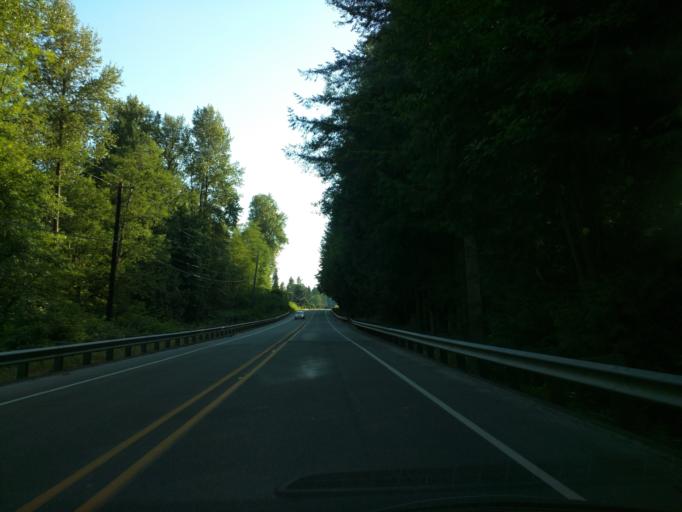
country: US
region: Washington
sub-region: Snohomish County
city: Arlington Heights
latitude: 48.2312
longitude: -122.0774
